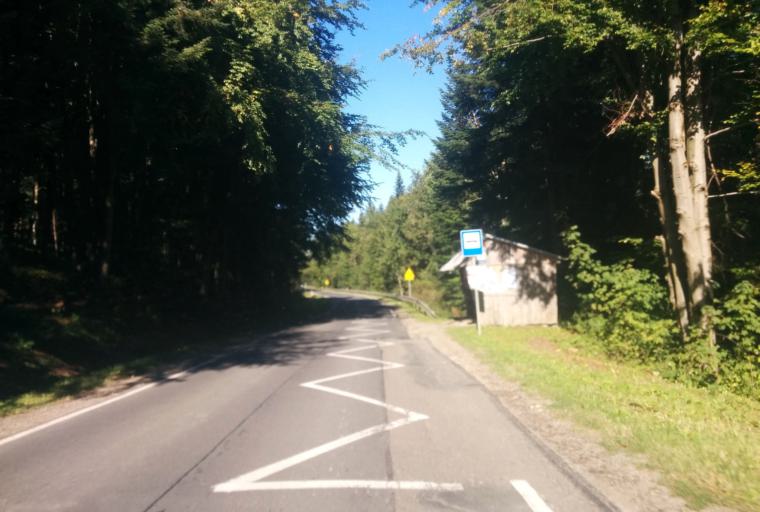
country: PL
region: Subcarpathian Voivodeship
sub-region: Powiat bieszczadzki
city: Lutowiska
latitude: 49.2900
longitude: 22.6755
